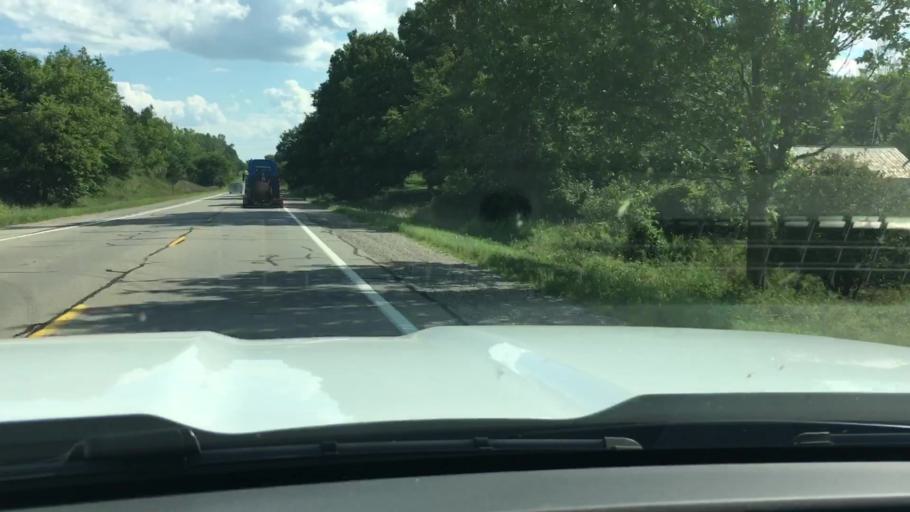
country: US
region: Michigan
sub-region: Ionia County
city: Ionia
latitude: 43.1342
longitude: -85.0747
